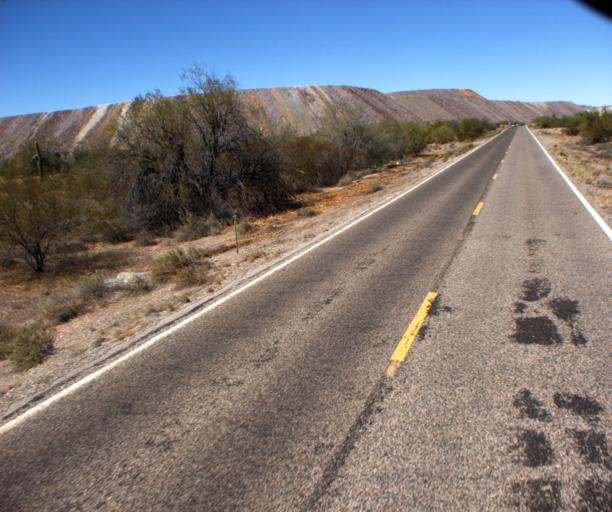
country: US
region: Arizona
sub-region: Pima County
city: Ajo
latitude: 32.3539
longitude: -112.8234
